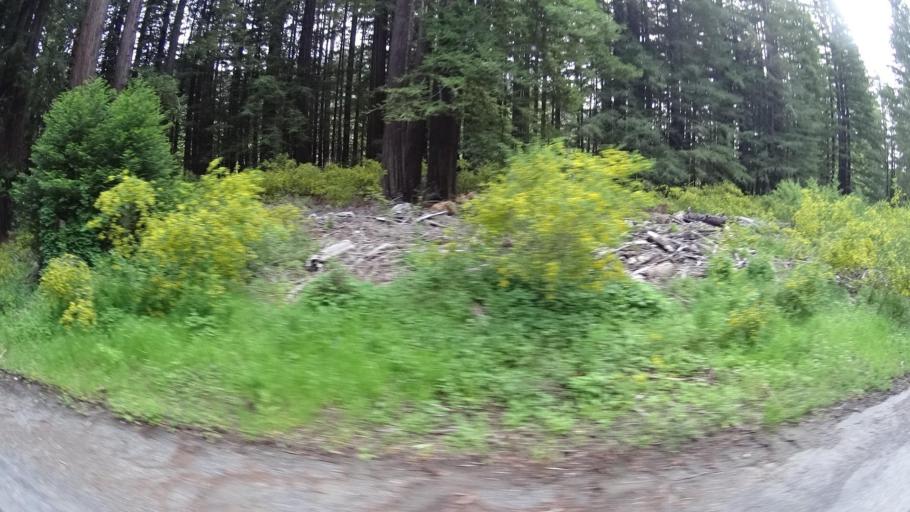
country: US
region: California
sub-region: Humboldt County
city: Redway
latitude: 40.3289
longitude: -123.8438
